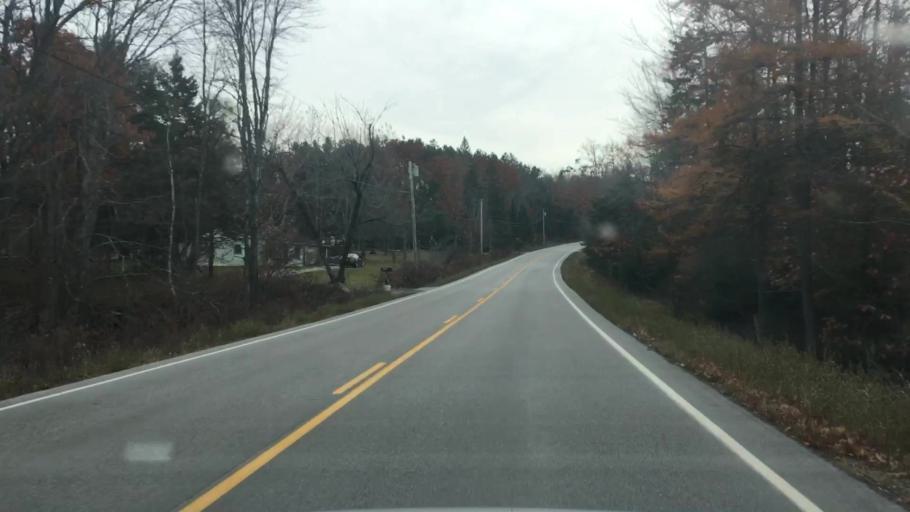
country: US
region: Maine
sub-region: Hancock County
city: Penobscot
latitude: 44.5011
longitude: -68.6512
